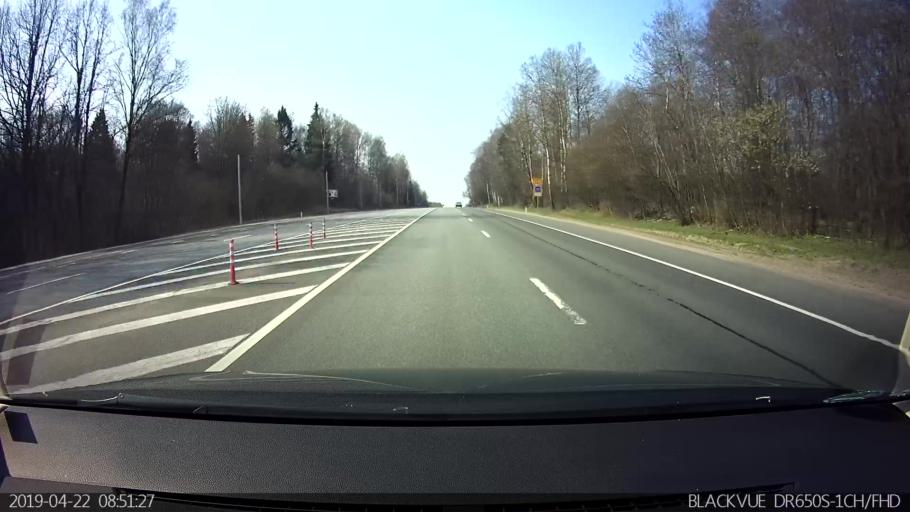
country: RU
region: Smolensk
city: Pechersk
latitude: 54.9234
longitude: 32.1434
